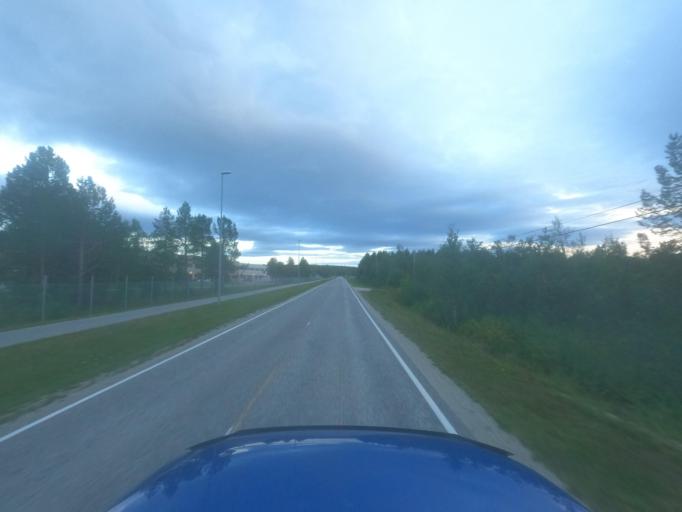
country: NO
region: Finnmark Fylke
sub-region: Porsanger
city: Lakselv
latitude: 69.9066
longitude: 24.9975
